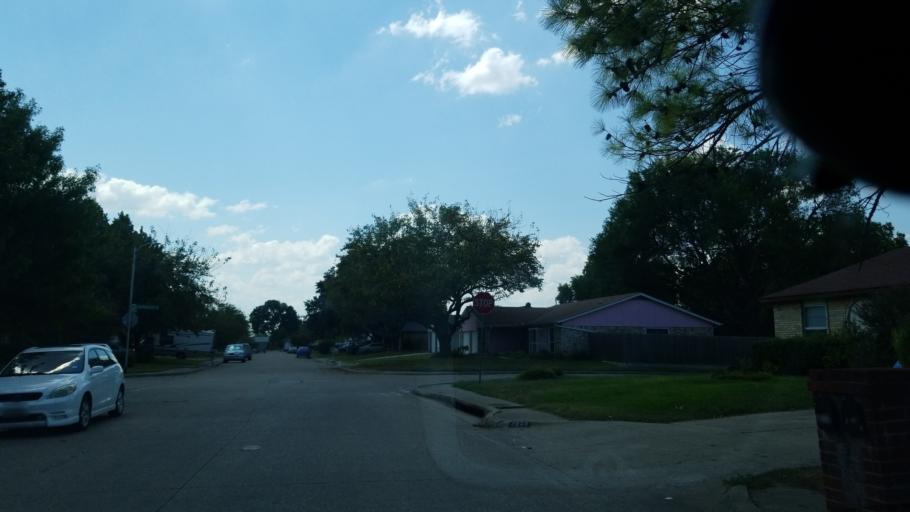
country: US
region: Texas
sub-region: Dallas County
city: Grand Prairie
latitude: 32.7130
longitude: -96.9924
